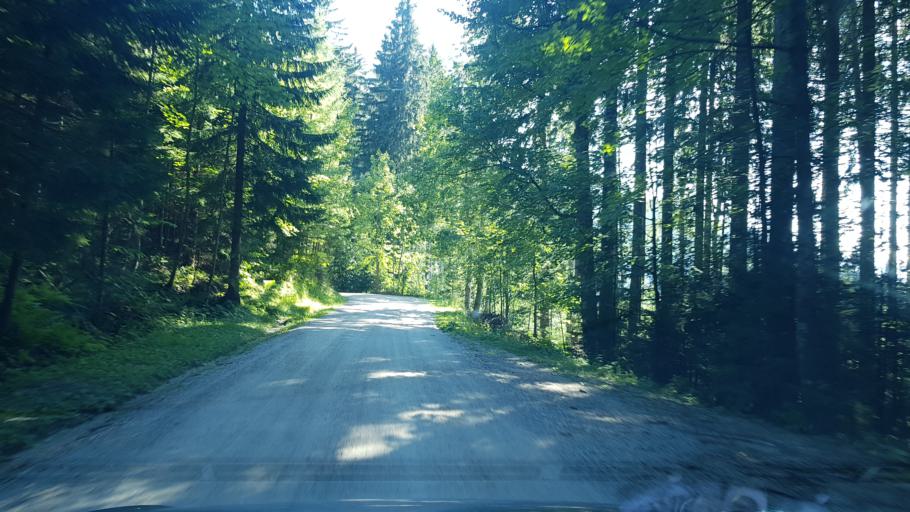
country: SI
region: Ravne na Koroskem
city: Kotlje
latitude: 46.4889
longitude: 14.9420
